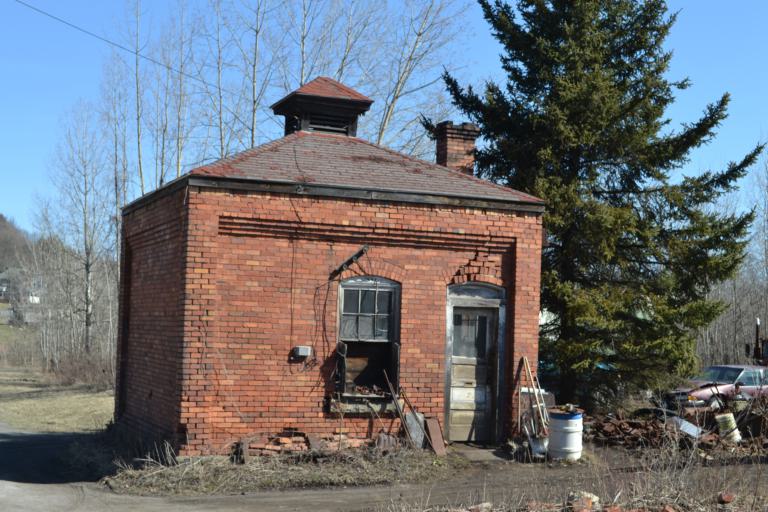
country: US
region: Pennsylvania
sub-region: Jefferson County
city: Sykesville
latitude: 41.0438
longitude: -78.8261
